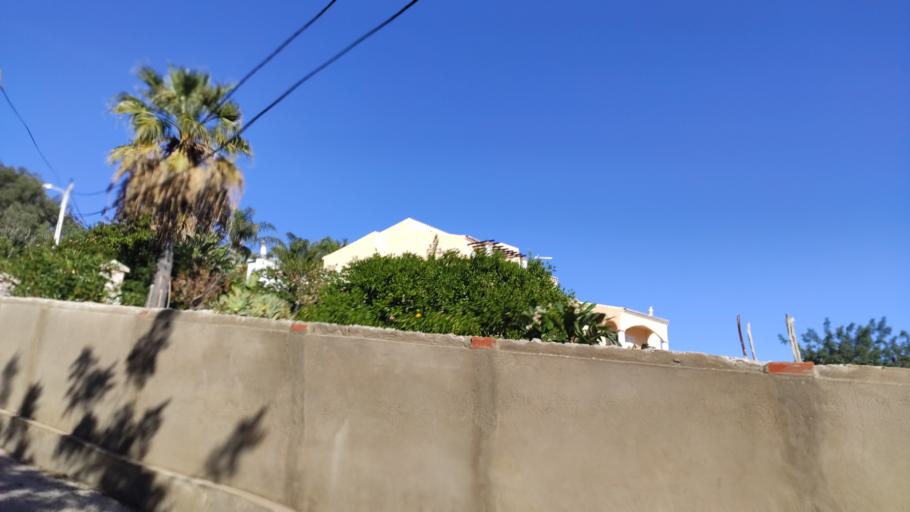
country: PT
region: Faro
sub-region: Sao Bras de Alportel
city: Sao Bras de Alportel
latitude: 37.1553
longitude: -7.9080
